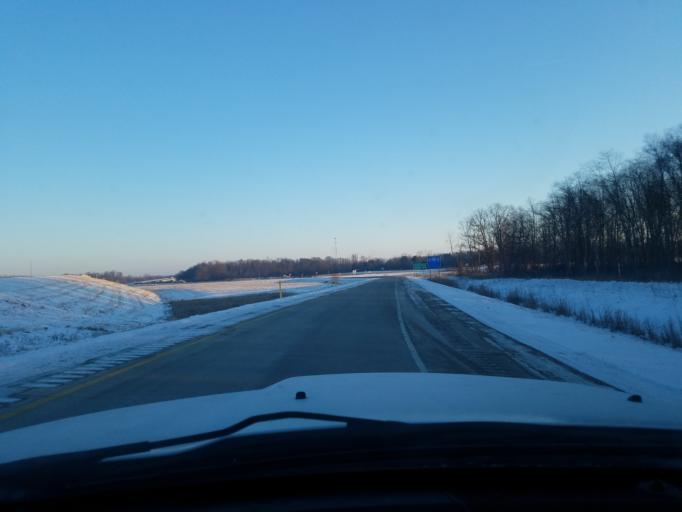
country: US
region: Indiana
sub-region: Marshall County
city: Plymouth
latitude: 41.4468
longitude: -86.2920
